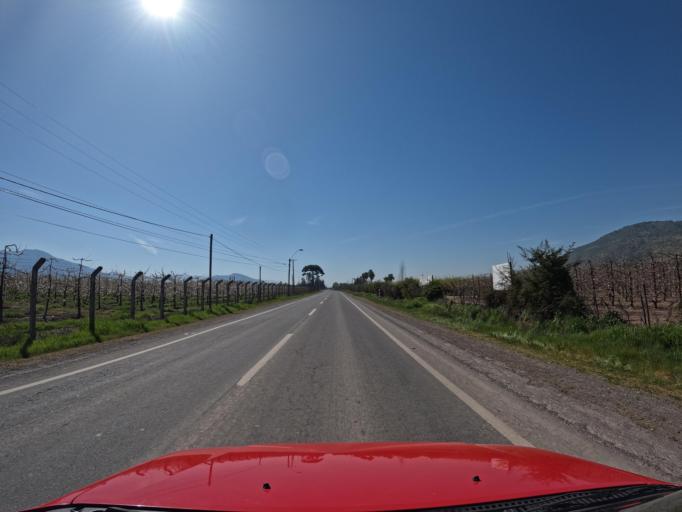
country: CL
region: Maule
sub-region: Provincia de Curico
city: Rauco
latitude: -35.0147
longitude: -71.4208
